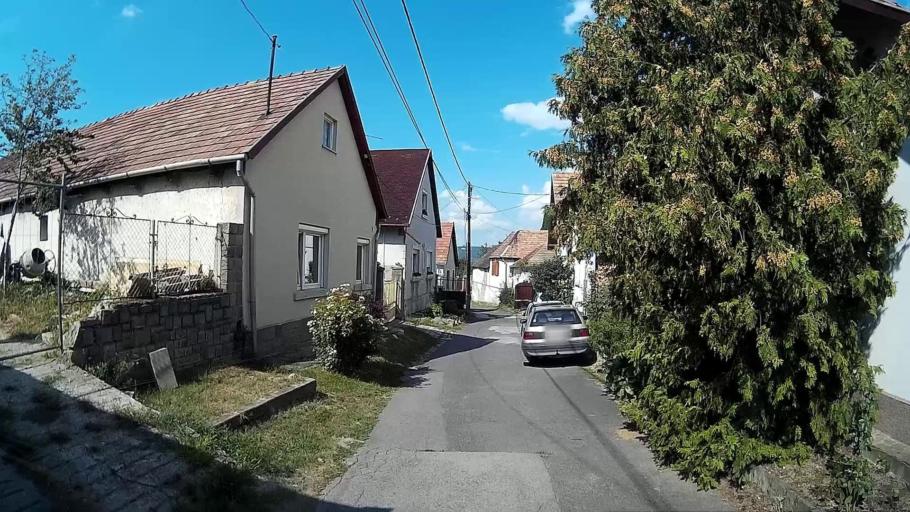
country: HU
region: Pest
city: Dunabogdany
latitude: 47.7932
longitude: 19.0285
